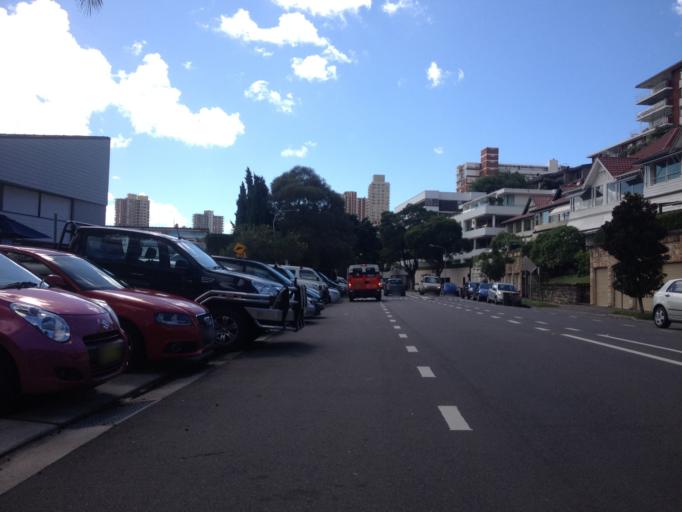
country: AU
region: New South Wales
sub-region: Woollahra
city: Darling Point
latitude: -33.8744
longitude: 151.2341
